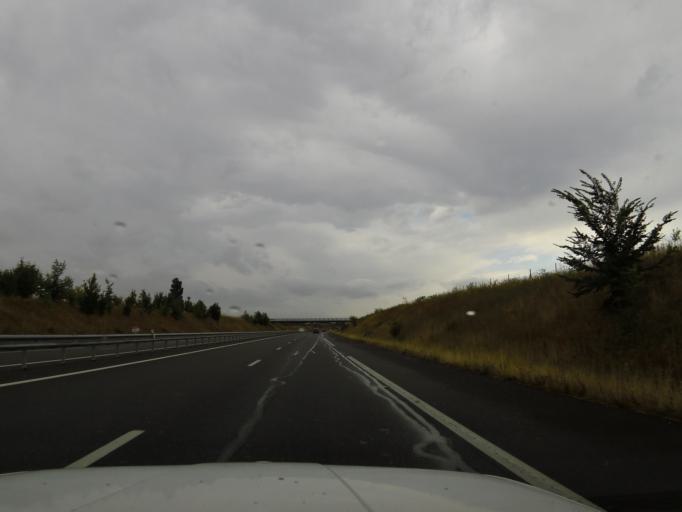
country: FR
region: Rhone-Alpes
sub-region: Departement de l'Isere
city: Janneyrias
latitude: 45.7538
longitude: 5.0927
